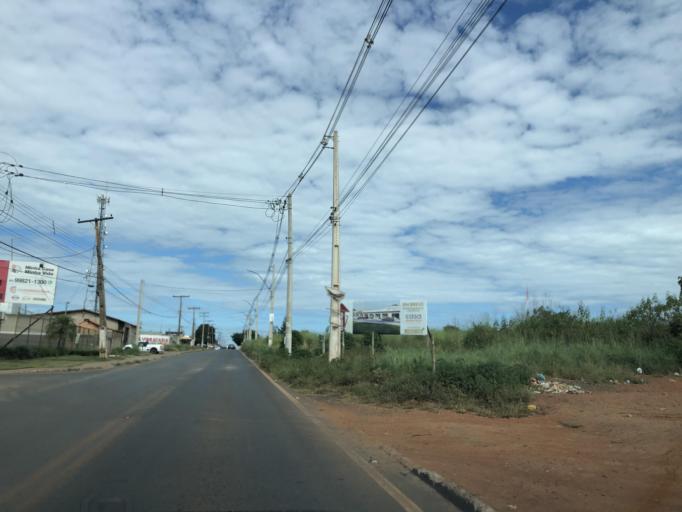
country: BR
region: Goias
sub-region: Luziania
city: Luziania
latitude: -16.1068
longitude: -47.9751
